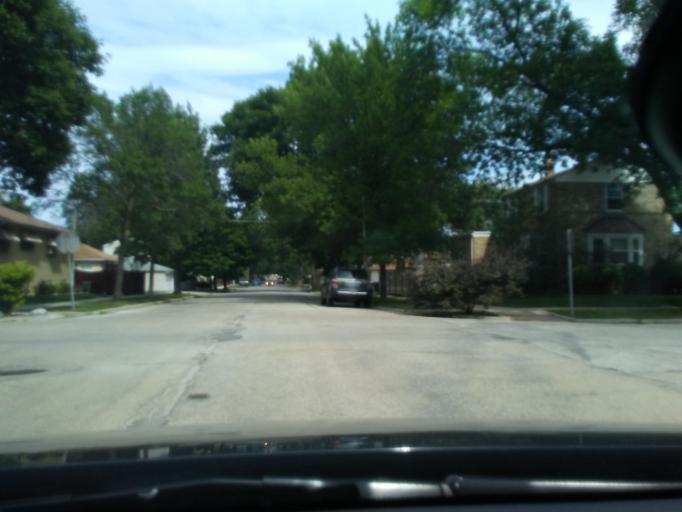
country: US
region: Illinois
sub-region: Cook County
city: Harwood Heights
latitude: 41.9738
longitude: -87.7929
